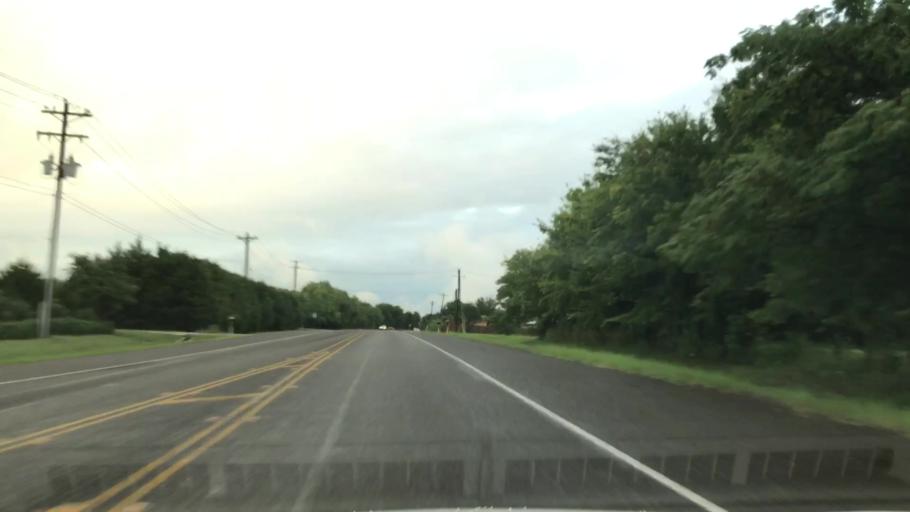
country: US
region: Texas
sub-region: Rockwall County
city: Rockwall
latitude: 32.9720
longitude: -96.4662
